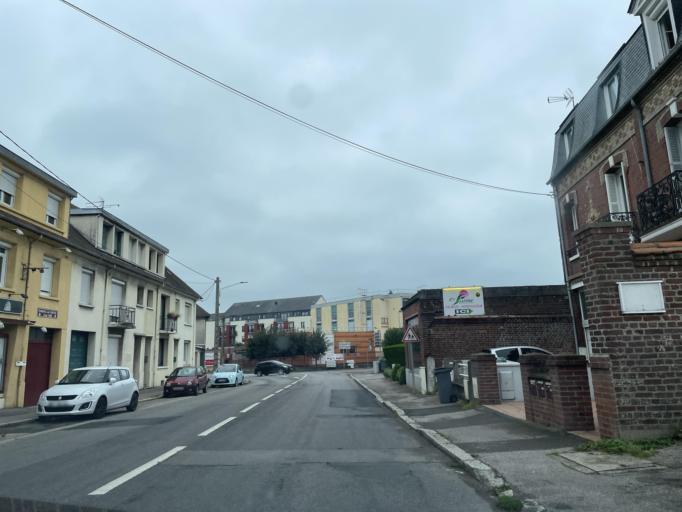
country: FR
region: Haute-Normandie
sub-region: Departement de la Seine-Maritime
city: Eu
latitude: 50.0443
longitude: 1.4228
